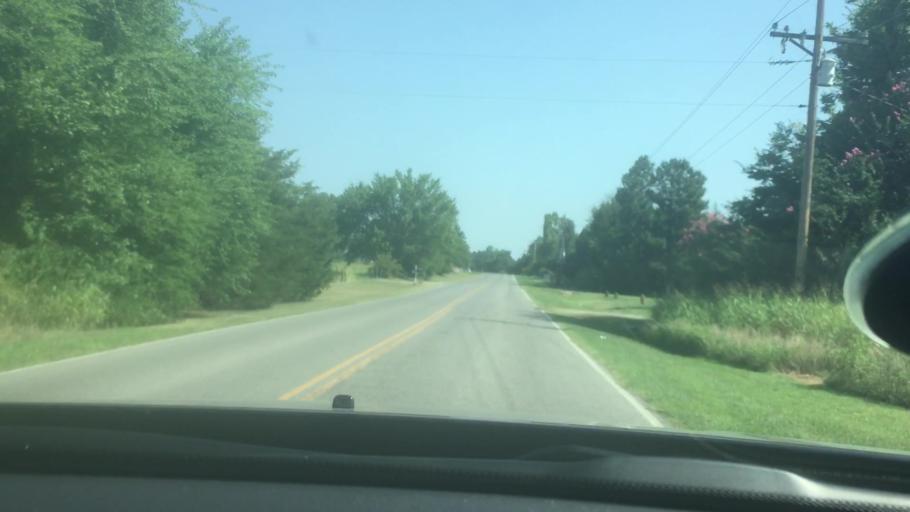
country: US
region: Oklahoma
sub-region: Bryan County
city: Calera
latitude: 34.0233
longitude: -96.4742
